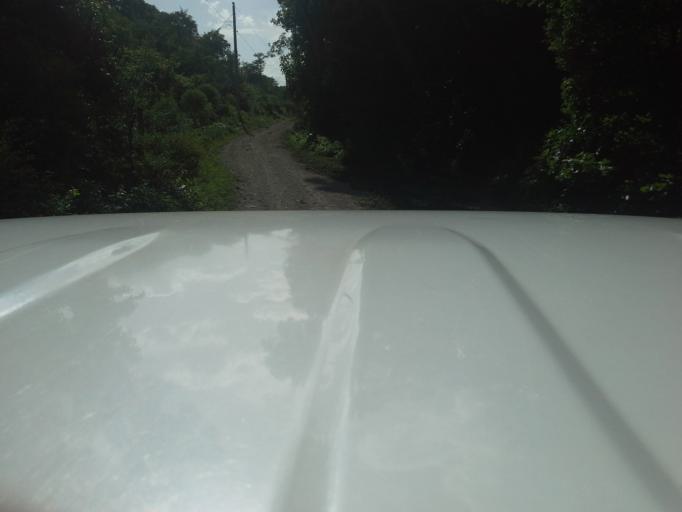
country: NI
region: Matagalpa
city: Terrabona
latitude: 12.6676
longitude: -86.0434
